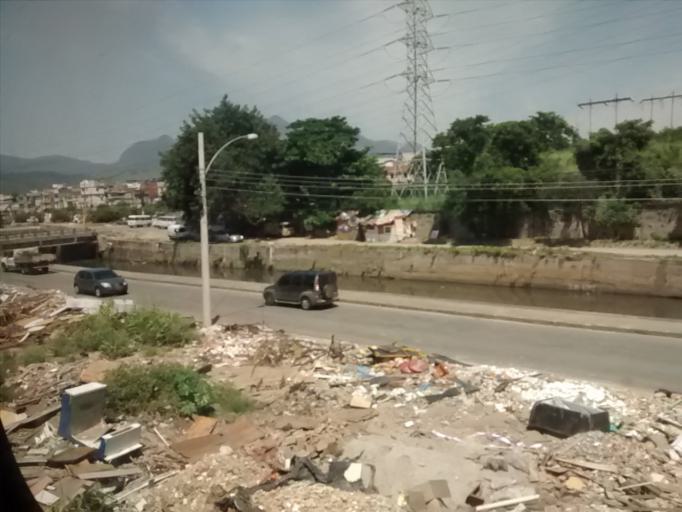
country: BR
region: Rio de Janeiro
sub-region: Rio De Janeiro
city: Rio de Janeiro
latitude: -22.8743
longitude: -43.2534
